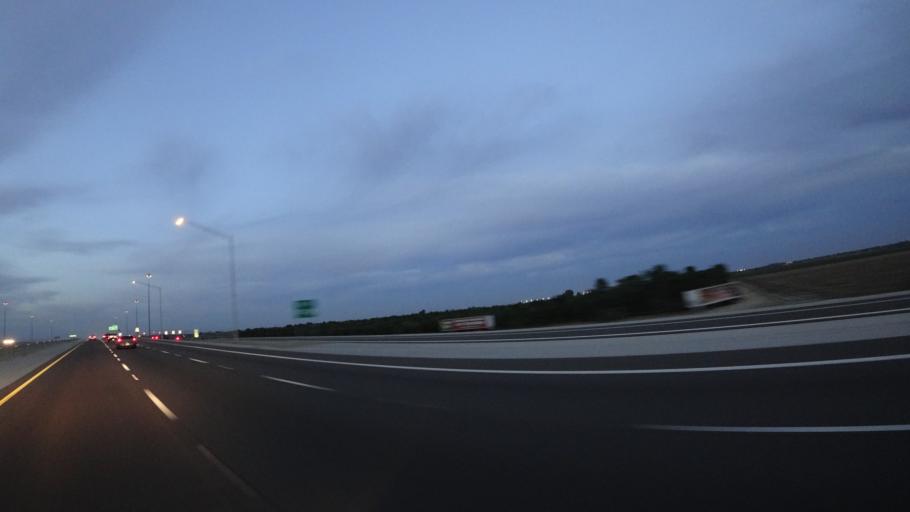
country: US
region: Arizona
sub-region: Maricopa County
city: Citrus Park
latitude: 33.5190
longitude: -112.4186
